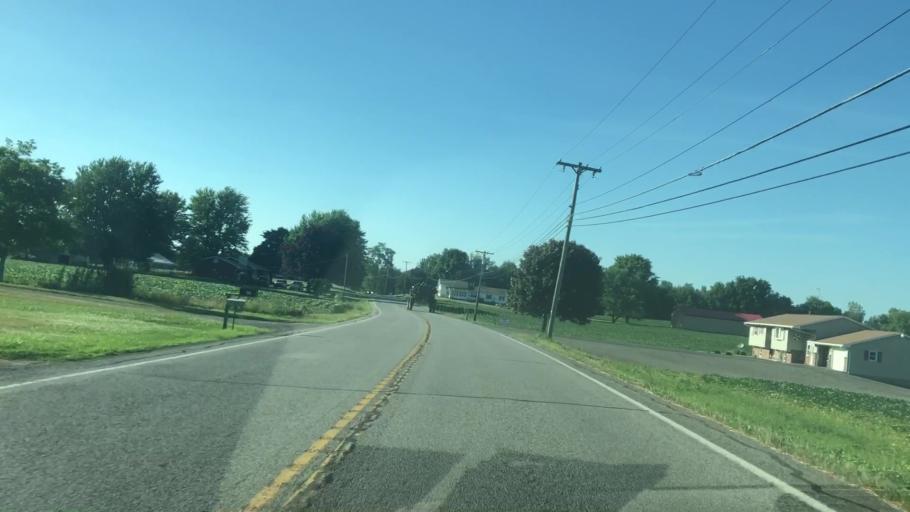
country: US
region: New York
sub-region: Wayne County
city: Ontario
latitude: 43.1900
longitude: -77.2919
